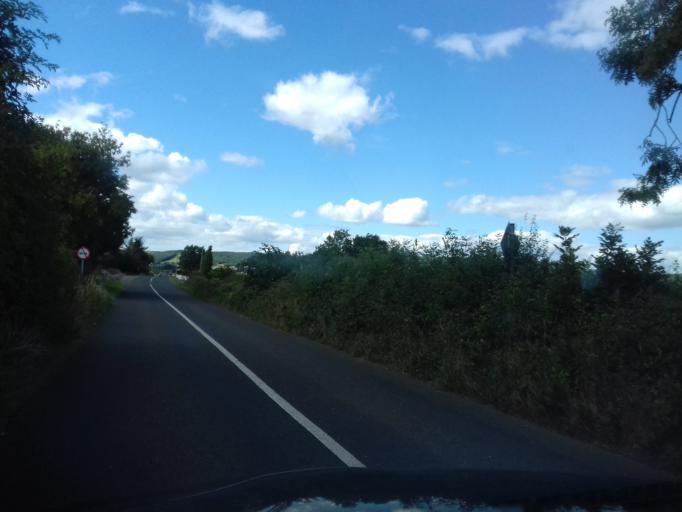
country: IE
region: Munster
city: Carrick-on-Suir
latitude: 52.3694
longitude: -7.4462
